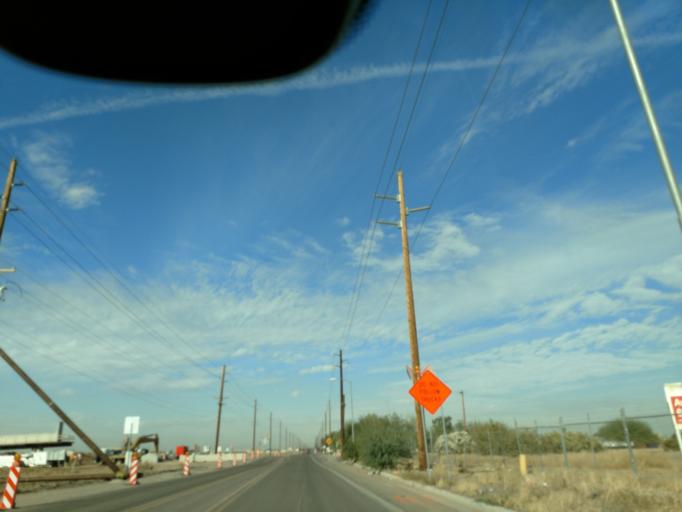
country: US
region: Arizona
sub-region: Maricopa County
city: Laveen
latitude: 33.4291
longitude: -112.1865
